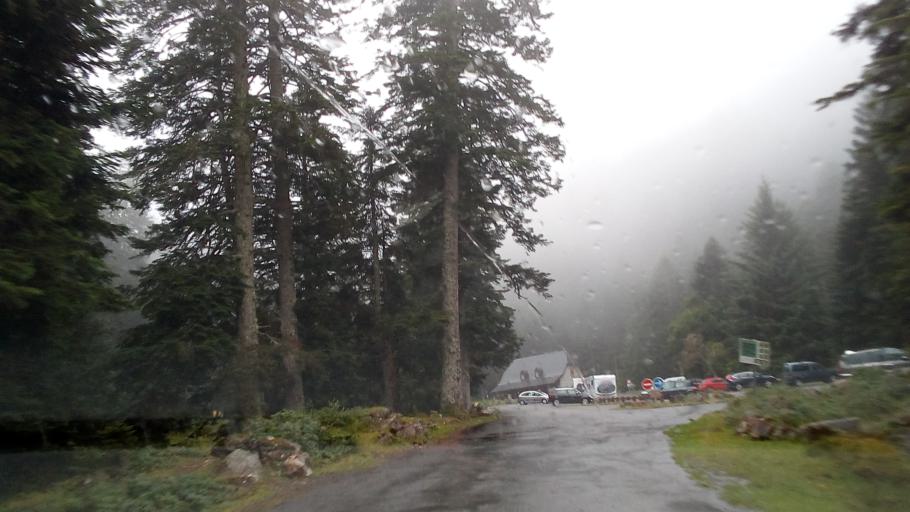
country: ES
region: Aragon
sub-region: Provincia de Huesca
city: Sallent de Gallego
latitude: 42.8850
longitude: -0.2699
